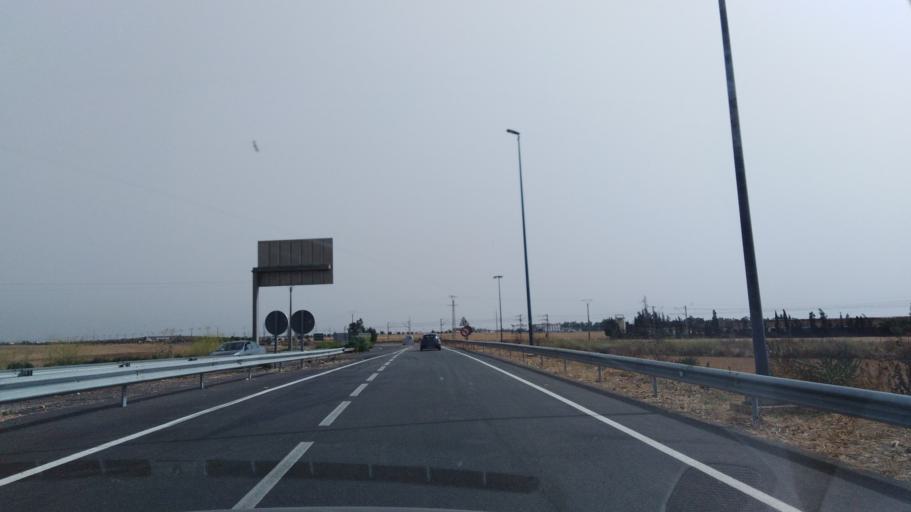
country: MA
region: Chaouia-Ouardigha
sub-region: Settat Province
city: Berrechid
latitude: 33.3155
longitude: -7.6031
